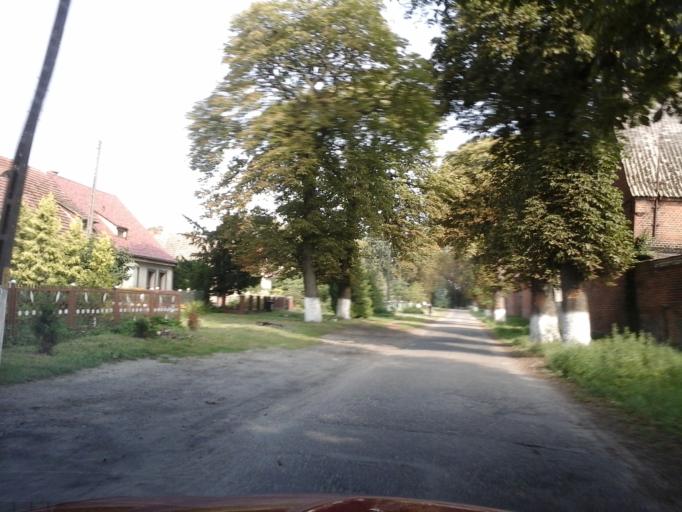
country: PL
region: West Pomeranian Voivodeship
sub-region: Powiat choszczenski
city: Pelczyce
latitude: 53.0632
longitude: 15.2440
